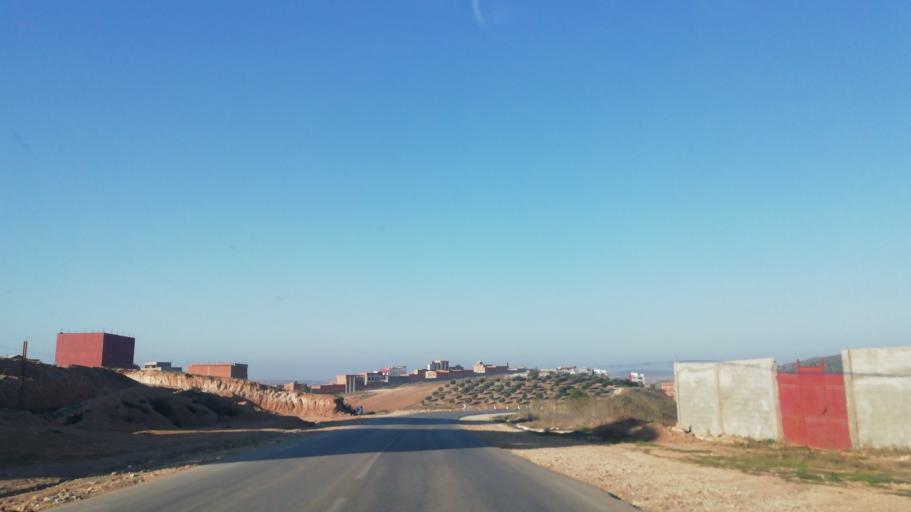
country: MA
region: Oriental
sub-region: Berkane-Taourirt
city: Ahfir
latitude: 35.0468
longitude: -2.1866
